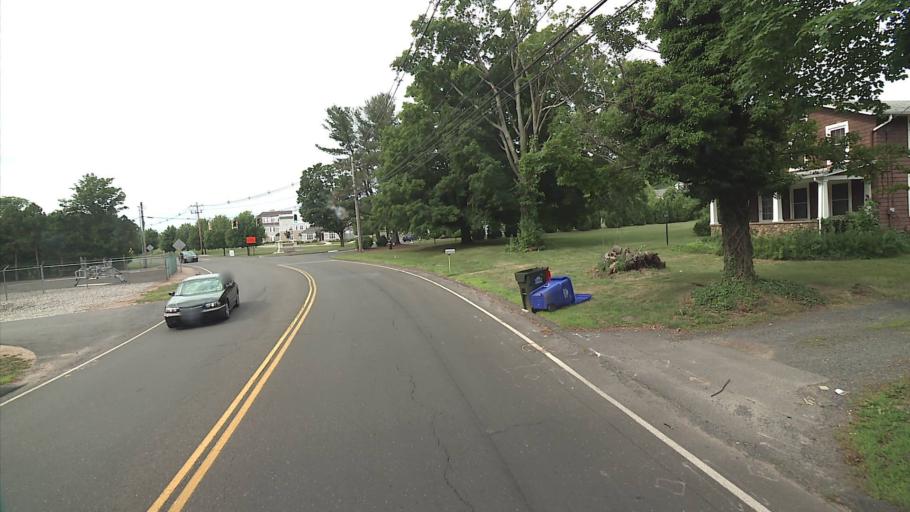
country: US
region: Connecticut
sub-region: New Haven County
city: Wallingford
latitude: 41.4657
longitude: -72.8344
